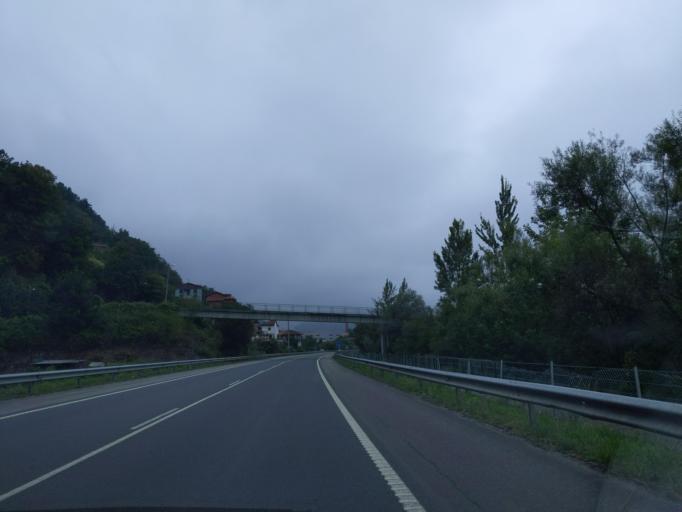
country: ES
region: Asturias
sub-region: Province of Asturias
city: Pola de Laviana
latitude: 43.2425
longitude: -5.5672
